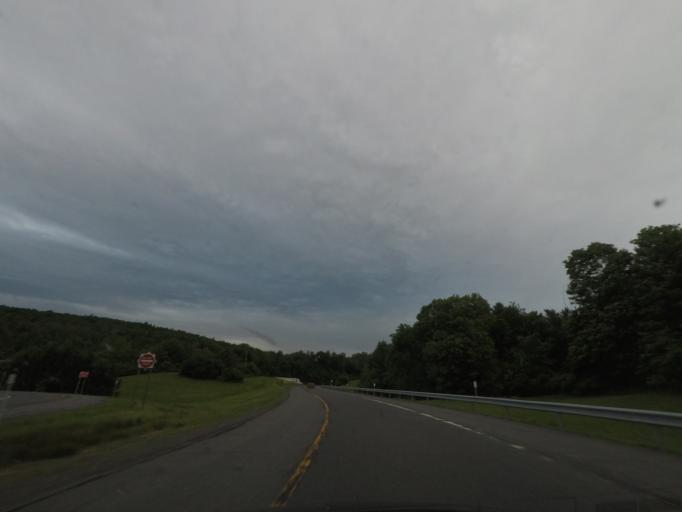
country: US
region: New York
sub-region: Columbia County
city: Chatham
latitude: 42.4233
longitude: -73.5482
